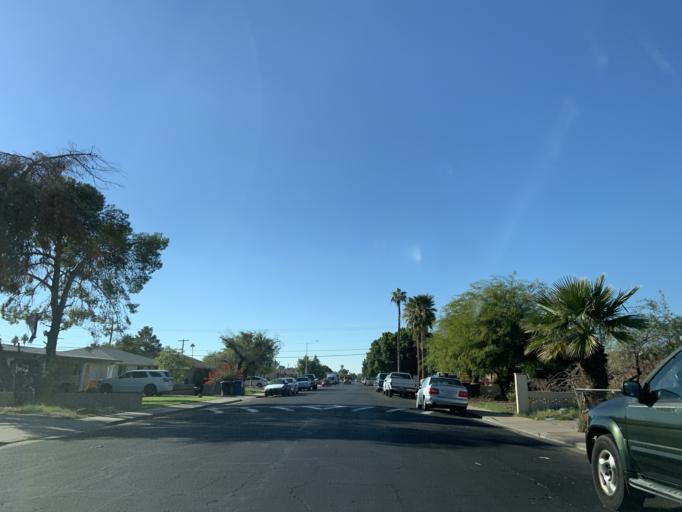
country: US
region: Arizona
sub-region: Maricopa County
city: Mesa
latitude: 33.4029
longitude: -111.8606
